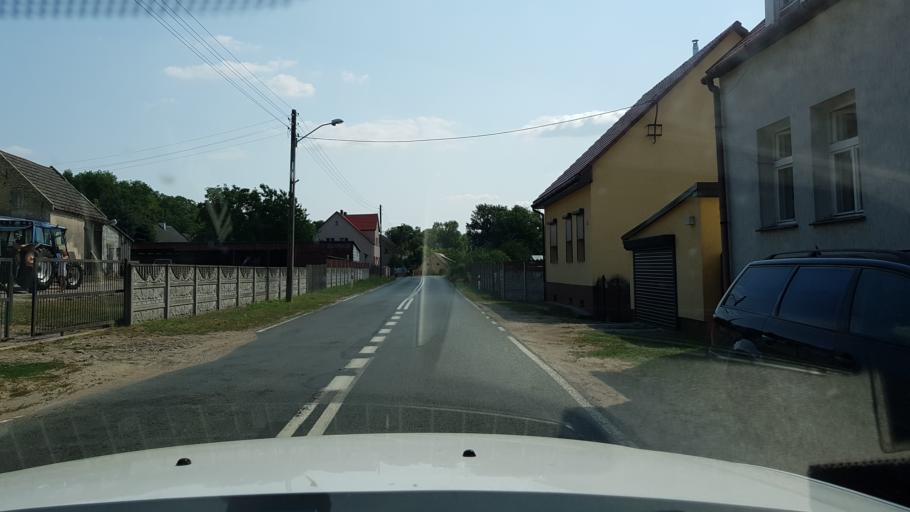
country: PL
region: West Pomeranian Voivodeship
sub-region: Powiat gryfinski
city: Cedynia
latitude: 52.8089
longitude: 14.2440
